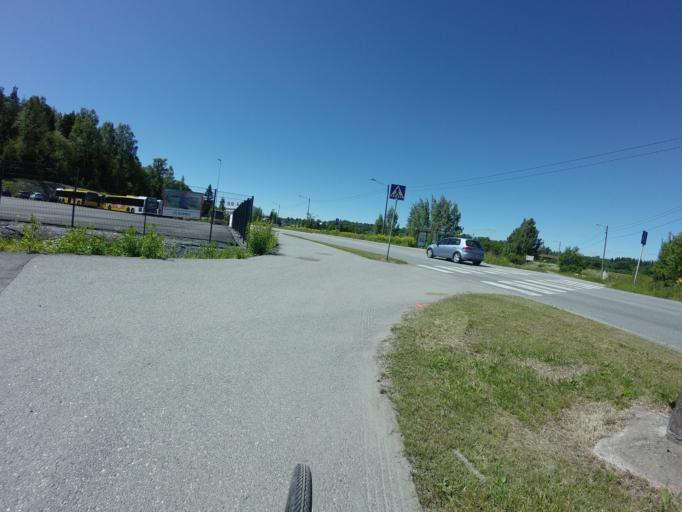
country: FI
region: Varsinais-Suomi
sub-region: Turku
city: Turku
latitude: 60.4817
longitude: 22.3037
